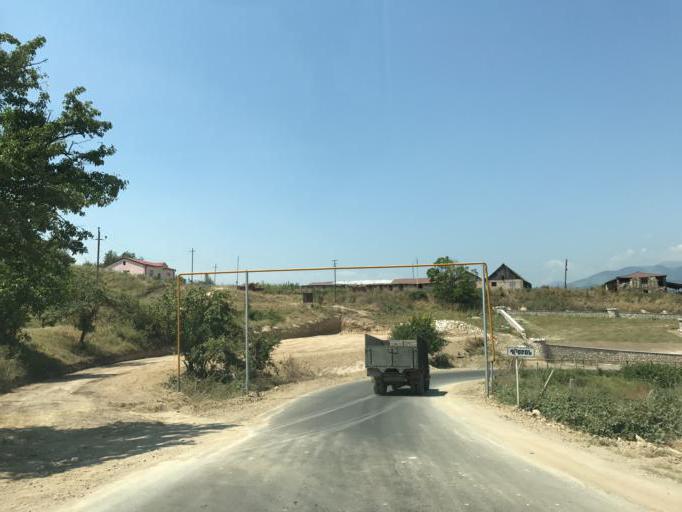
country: AZ
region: Tartar Rayon
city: Martakert
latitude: 40.1449
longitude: 46.6157
